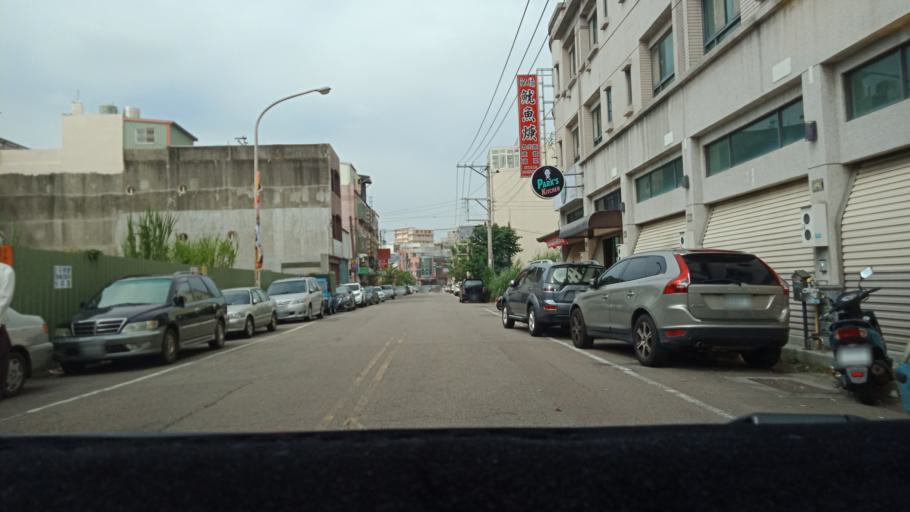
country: TW
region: Taiwan
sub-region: Hsinchu
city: Zhubei
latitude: 24.8743
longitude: 120.9970
